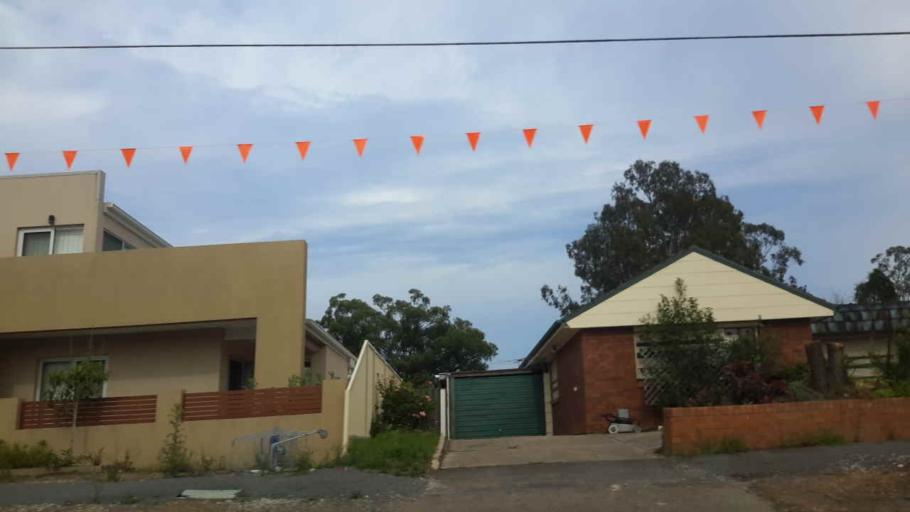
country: AU
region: New South Wales
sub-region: Penrith Municipality
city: Kingswood Park
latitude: -33.7668
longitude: 150.7098
